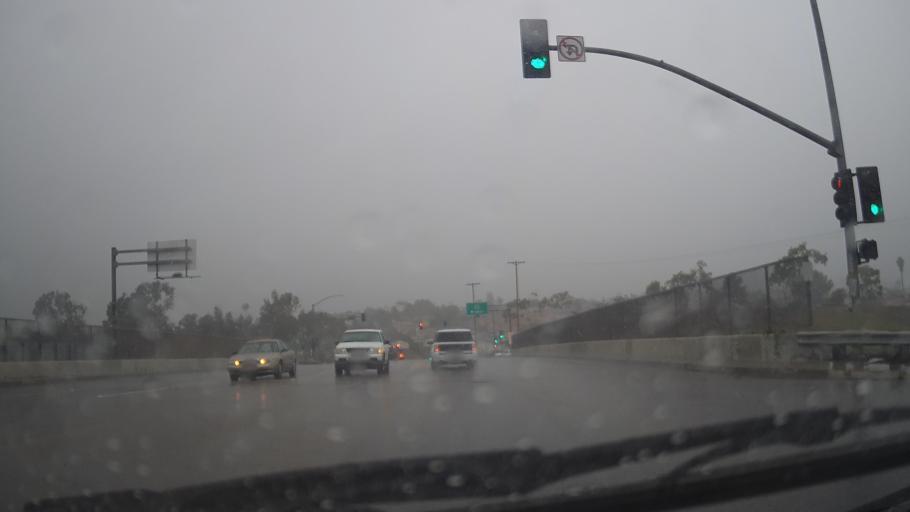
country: US
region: California
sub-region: San Diego County
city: Bonita
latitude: 32.6638
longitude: -117.0572
